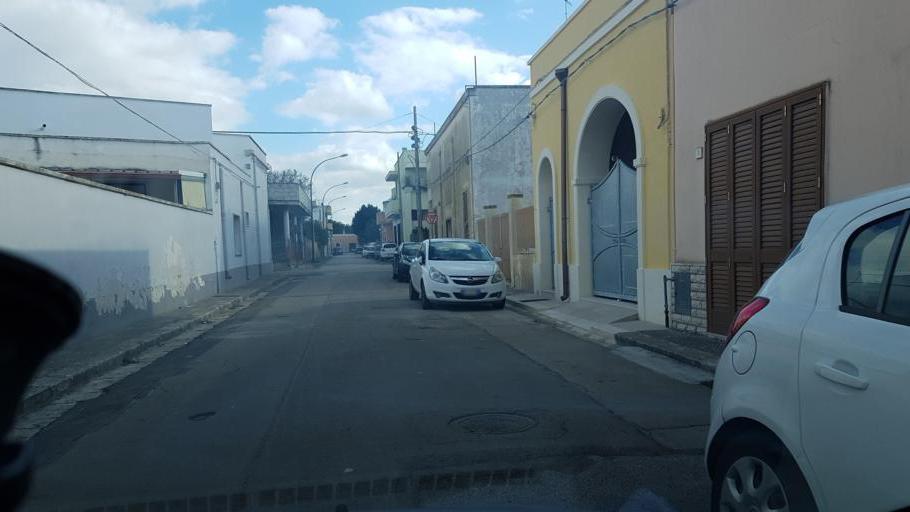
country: IT
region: Apulia
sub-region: Provincia di Lecce
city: Squinzano
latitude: 40.4417
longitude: 18.0384
